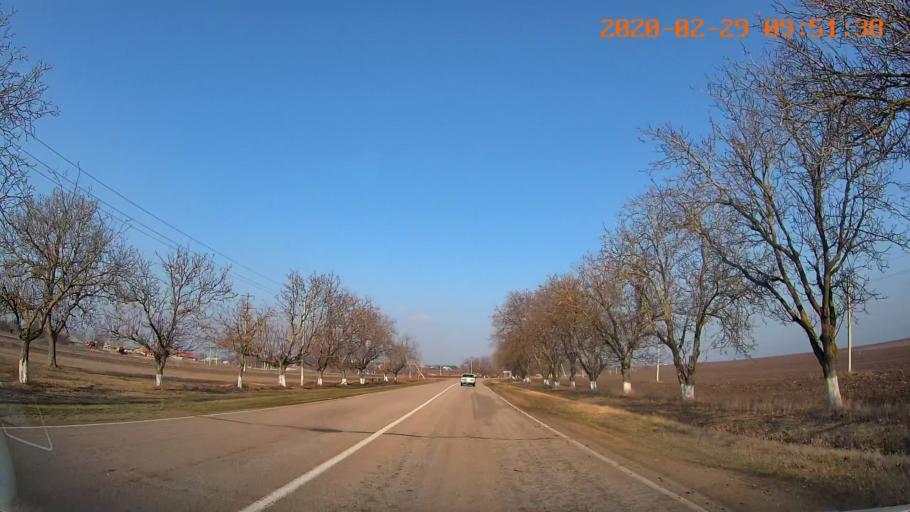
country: MD
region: Telenesti
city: Slobozia
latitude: 46.7101
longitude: 29.7370
